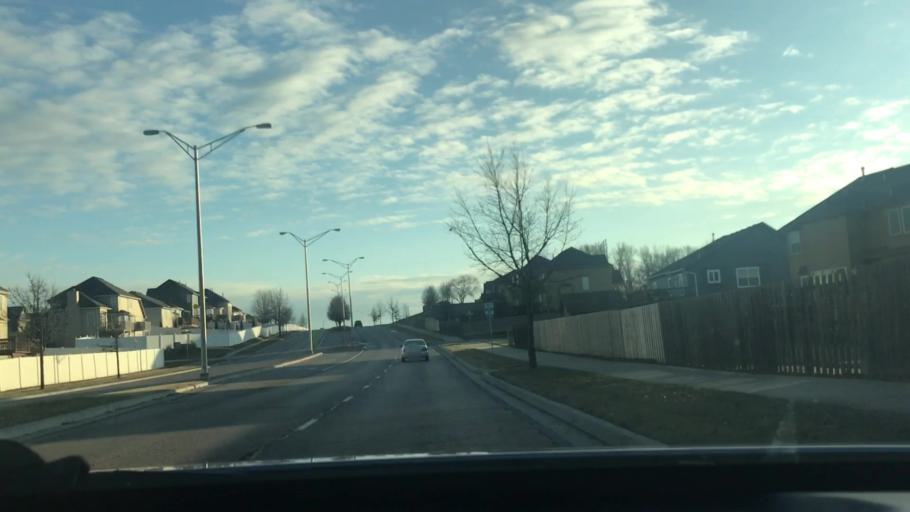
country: US
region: Missouri
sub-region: Jackson County
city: Lees Summit
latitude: 38.9386
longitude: -94.3438
